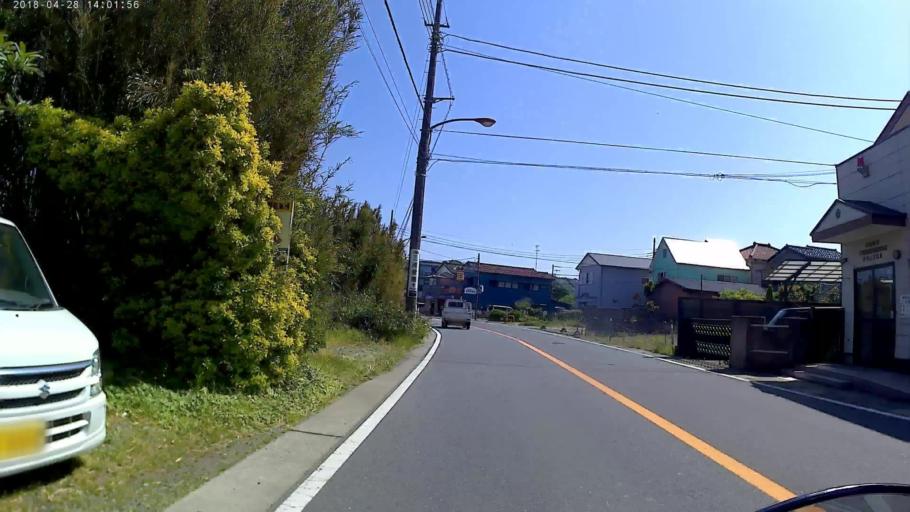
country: JP
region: Kanagawa
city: Miura
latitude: 35.1650
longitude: 139.6595
